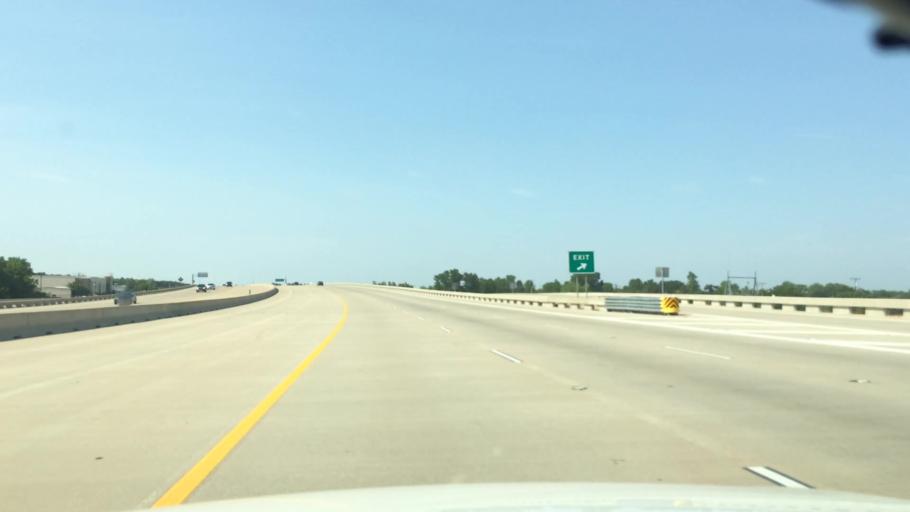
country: US
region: Texas
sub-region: Dallas County
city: Grand Prairie
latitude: 32.7890
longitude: -97.0188
